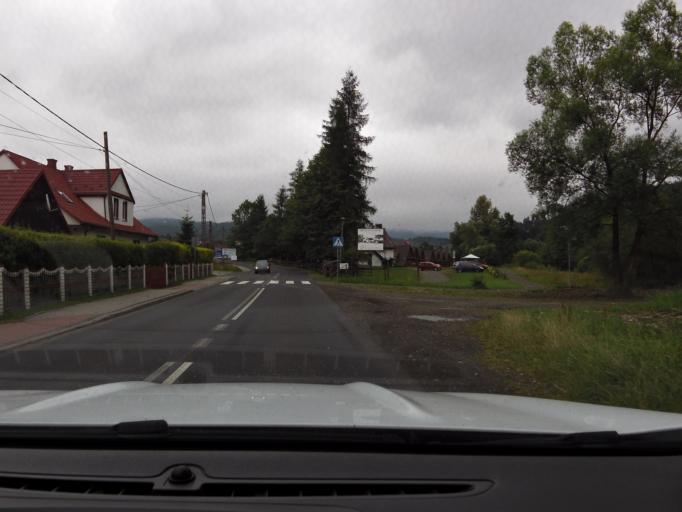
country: PL
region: Silesian Voivodeship
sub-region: Powiat zywiecki
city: Ujsoly
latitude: 49.4850
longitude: 19.1319
